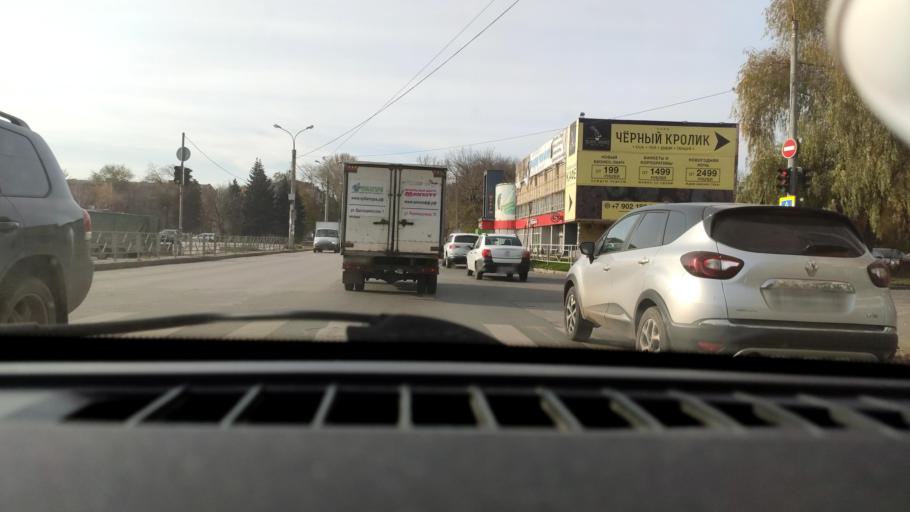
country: RU
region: Samara
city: Samara
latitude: 53.2151
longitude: 50.2581
